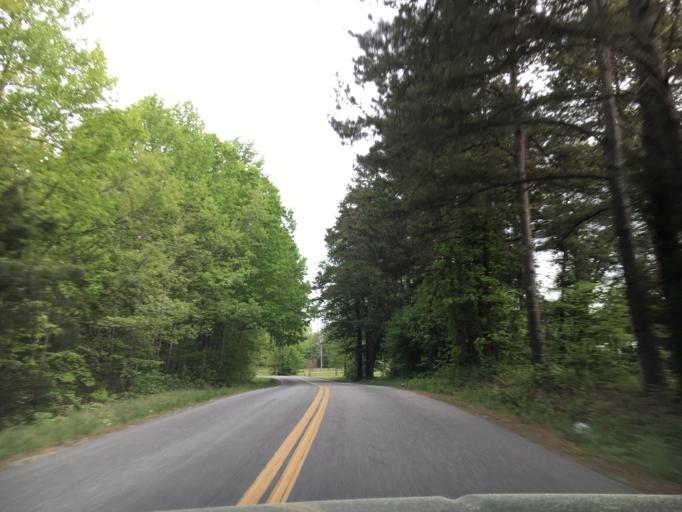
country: US
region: Virginia
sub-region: Campbell County
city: Brookneal
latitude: 36.9210
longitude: -78.9448
